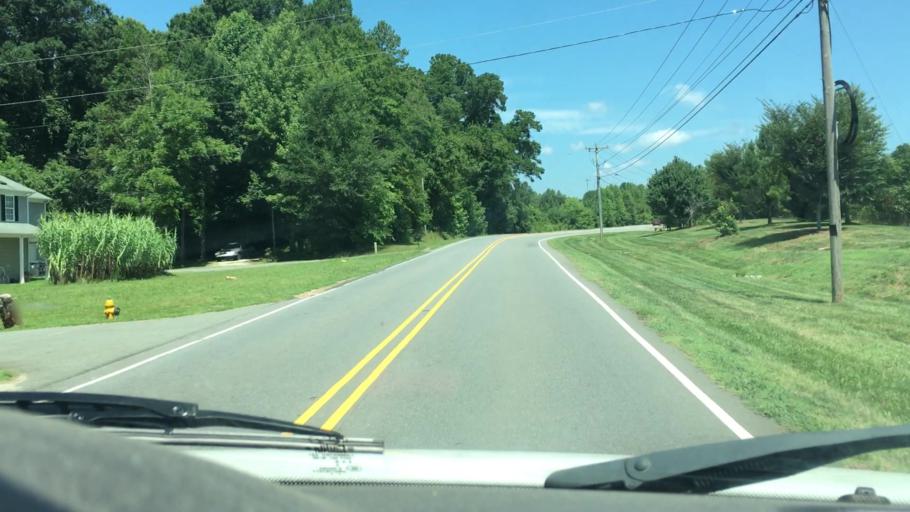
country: US
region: North Carolina
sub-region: Mecklenburg County
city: Huntersville
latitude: 35.3916
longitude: -80.9219
